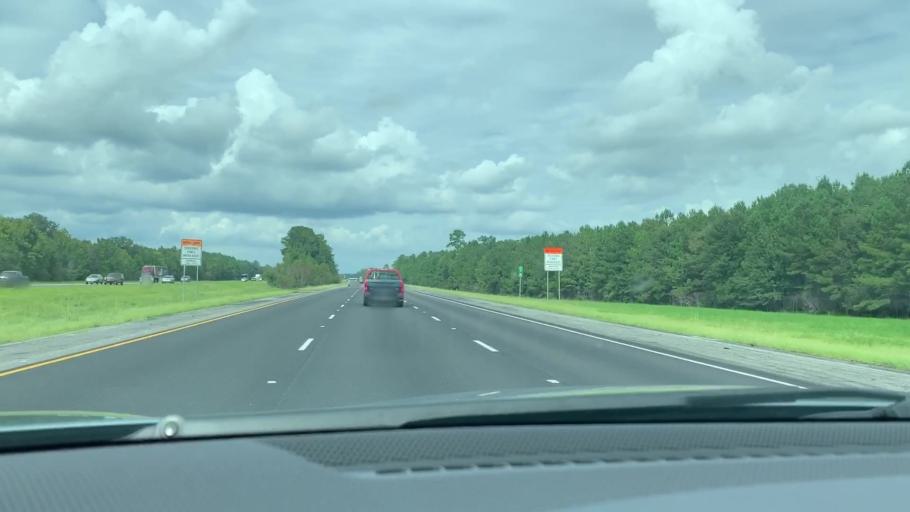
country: US
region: Georgia
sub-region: Liberty County
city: Midway
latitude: 31.7438
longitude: -81.3852
